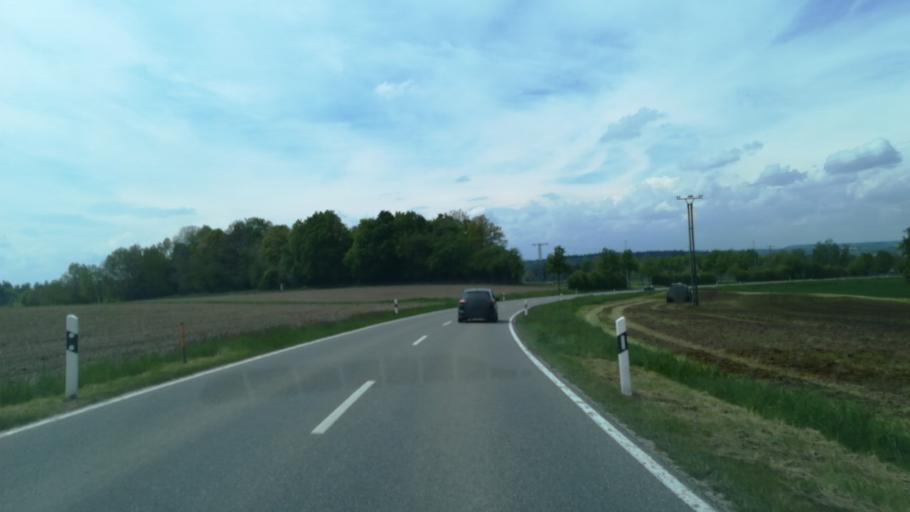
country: DE
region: Baden-Wuerttemberg
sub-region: Freiburg Region
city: Muhlingen
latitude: 47.8881
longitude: 9.0371
